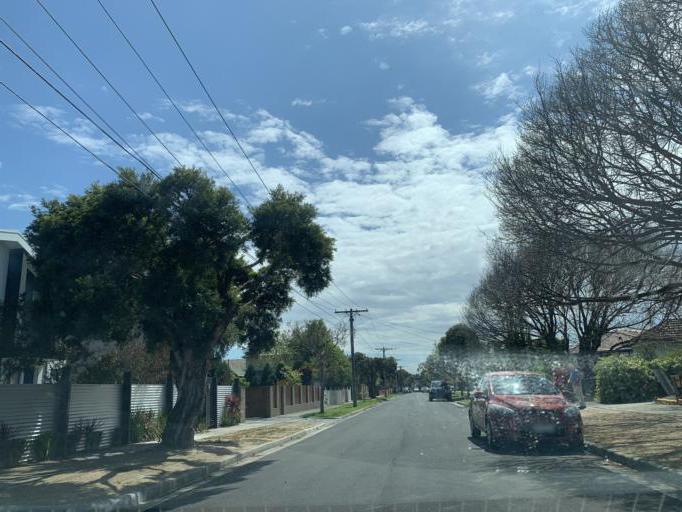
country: AU
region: Victoria
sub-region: Bayside
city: Hampton East
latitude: -37.9360
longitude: 145.0286
